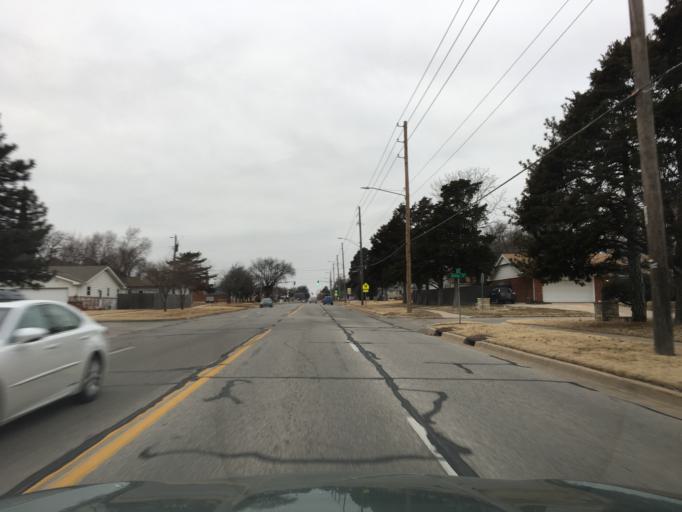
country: US
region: Kansas
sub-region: Sedgwick County
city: Bellaire
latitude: 37.7084
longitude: -97.2571
